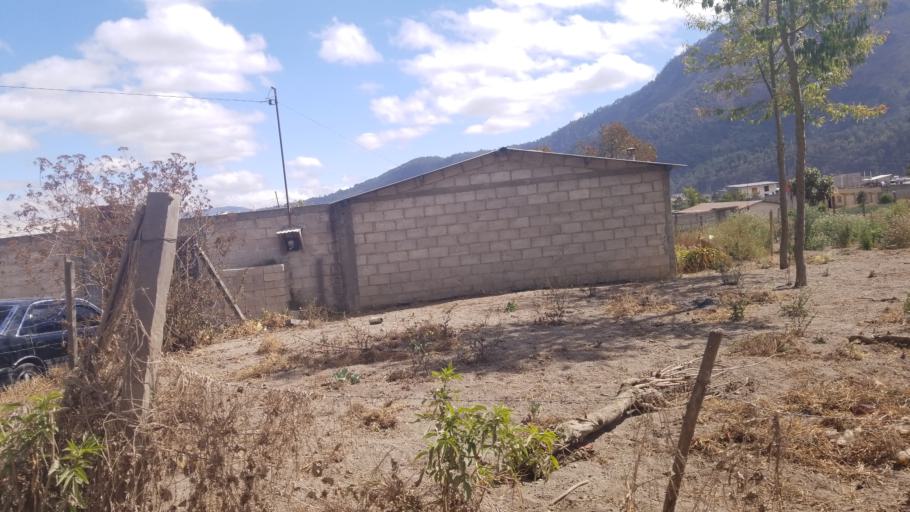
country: GT
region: Quetzaltenango
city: Almolonga
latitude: 14.7869
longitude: -91.5466
